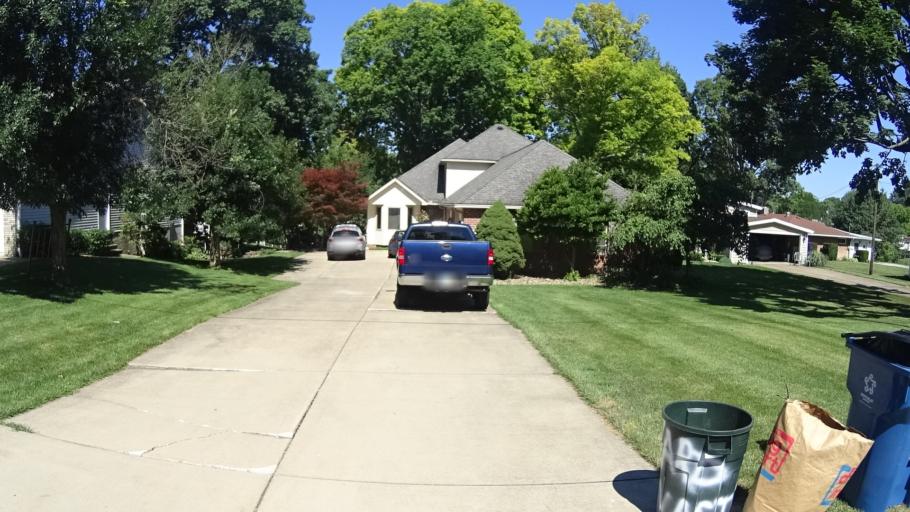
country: US
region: Ohio
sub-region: Erie County
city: Huron
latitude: 41.3768
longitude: -82.5580
